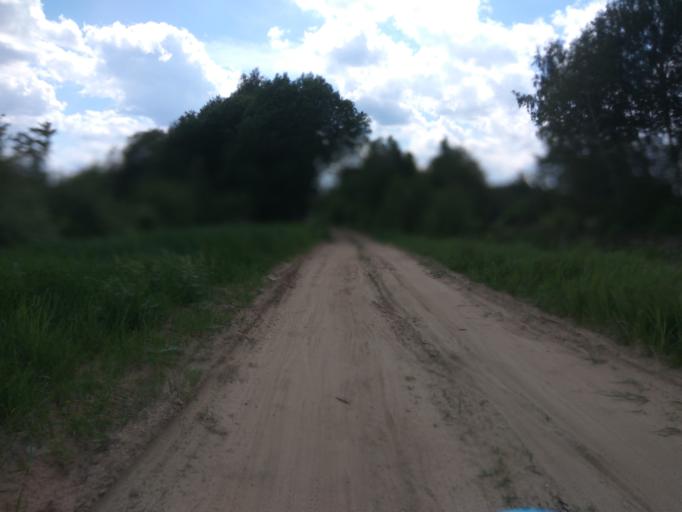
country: LV
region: Kuldigas Rajons
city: Kuldiga
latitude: 56.8876
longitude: 21.9729
